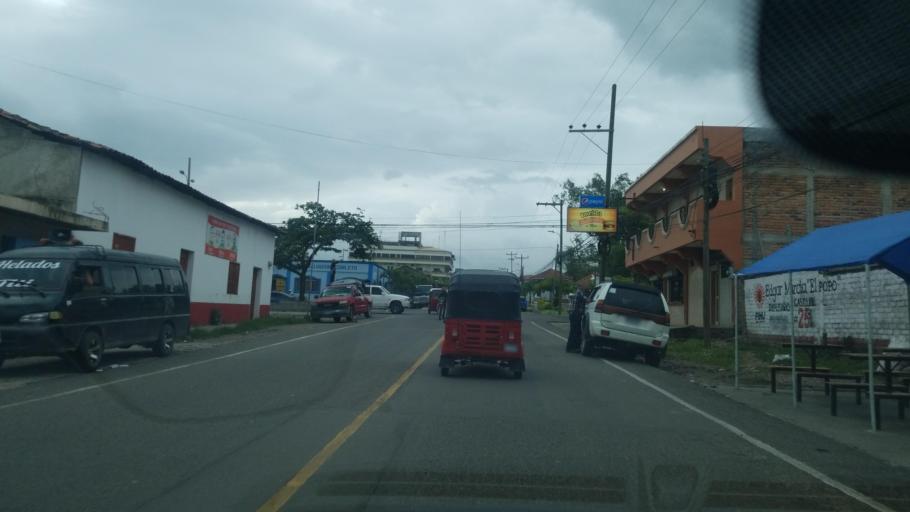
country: HN
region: Ocotepeque
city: Nueva Ocotepeque
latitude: 14.4333
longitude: -89.1828
